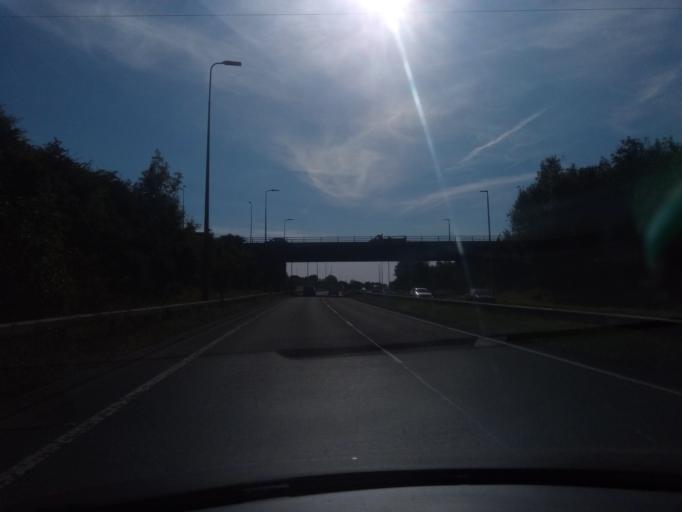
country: GB
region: England
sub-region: County Durham
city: Hawthorn
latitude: 54.7970
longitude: -1.3632
